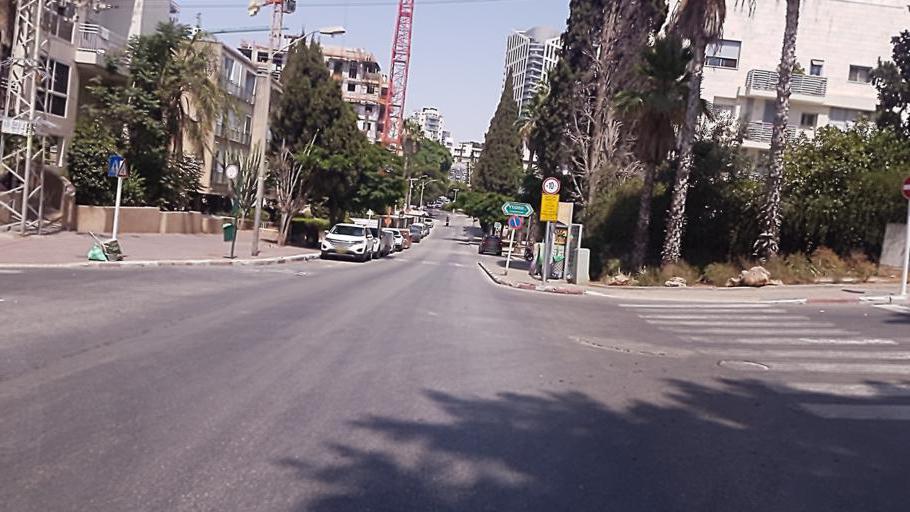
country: IL
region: Tel Aviv
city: Ramat Gan
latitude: 32.0786
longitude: 34.8076
